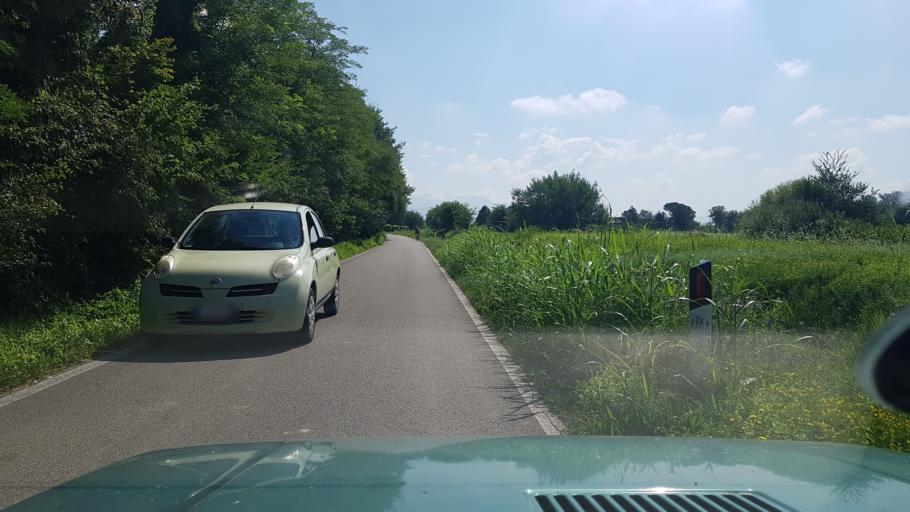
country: IT
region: Friuli Venezia Giulia
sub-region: Provincia di Gorizia
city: Mossa
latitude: 45.9369
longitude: 13.5370
